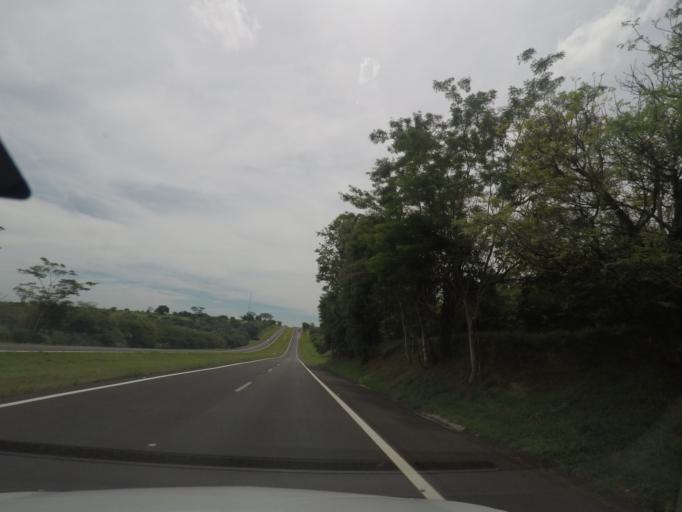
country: BR
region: Sao Paulo
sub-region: Bebedouro
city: Bebedouro
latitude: -20.9735
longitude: -48.4392
